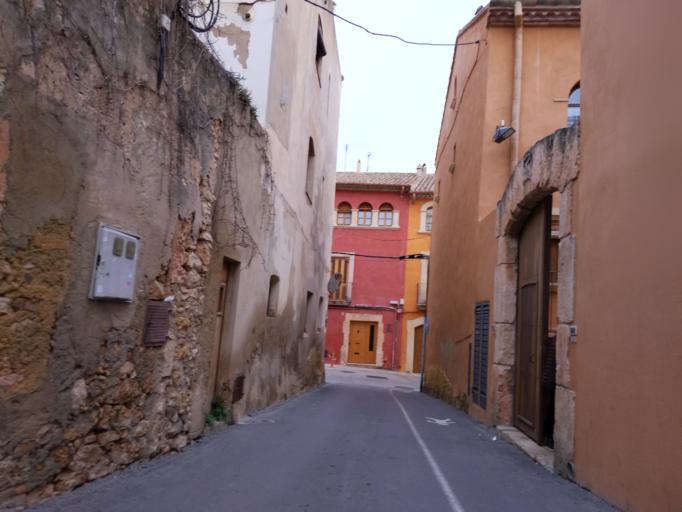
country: ES
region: Catalonia
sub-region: Provincia de Tarragona
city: Altafulla
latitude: 41.1416
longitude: 1.3751
